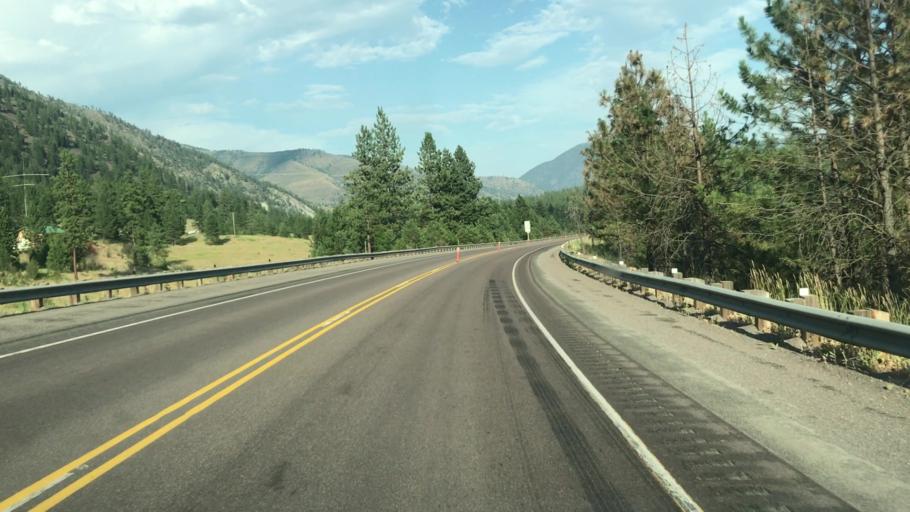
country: US
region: Montana
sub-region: Mineral County
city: Superior
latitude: 47.0186
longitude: -114.6779
